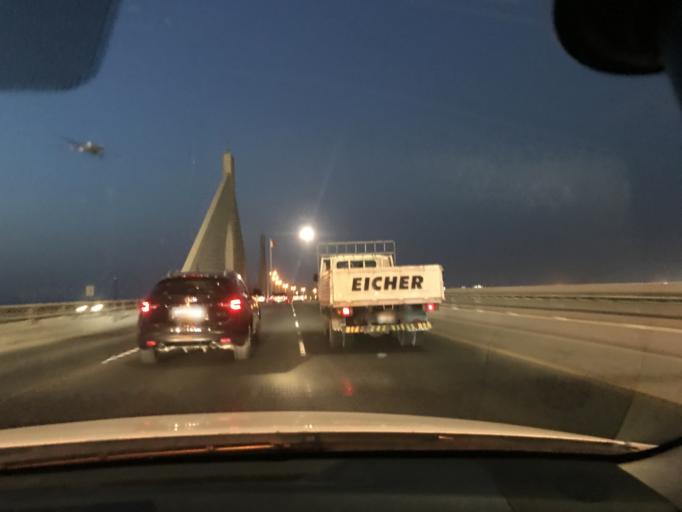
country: BH
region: Muharraq
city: Al Muharraq
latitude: 26.2520
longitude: 50.5931
